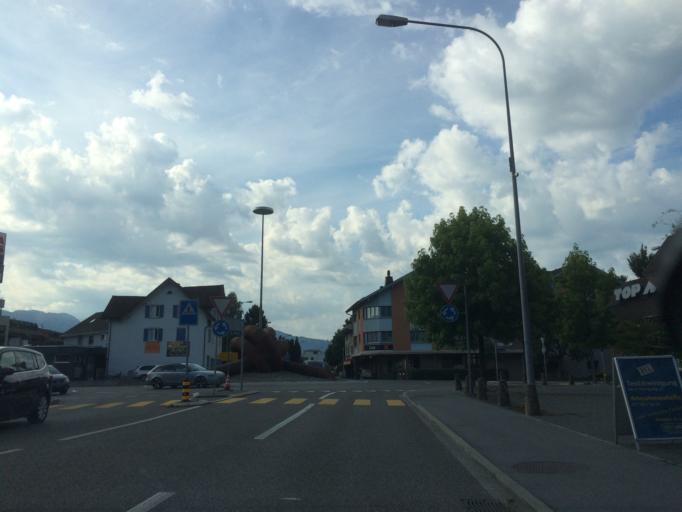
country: CH
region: Saint Gallen
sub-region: Wahlkreis Rheintal
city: Au
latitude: 47.4314
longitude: 9.6342
